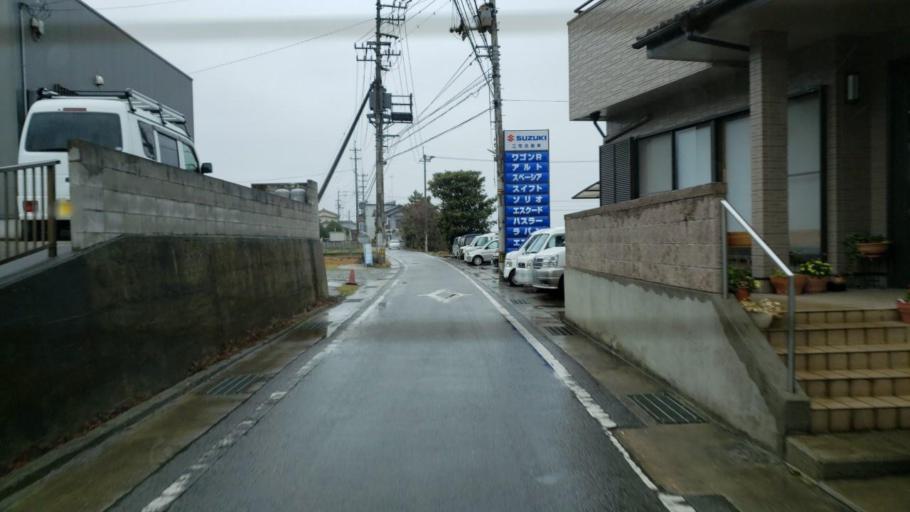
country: JP
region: Tokushima
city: Kamojimacho-jogejima
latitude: 34.0585
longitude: 134.3163
